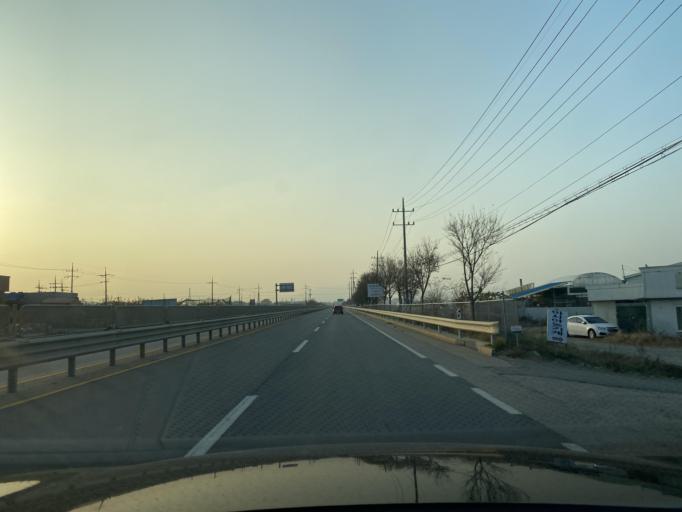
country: KR
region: Chungcheongnam-do
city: Yesan
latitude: 36.6862
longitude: 126.7707
